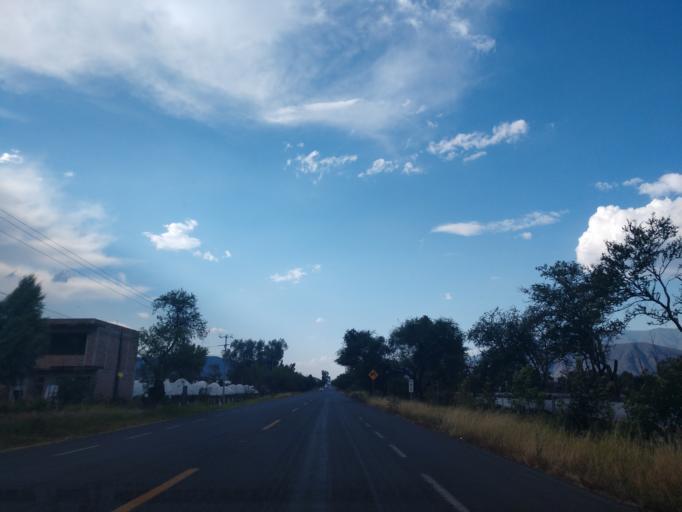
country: MX
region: Jalisco
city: Jocotepec
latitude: 20.2336
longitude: -103.4219
